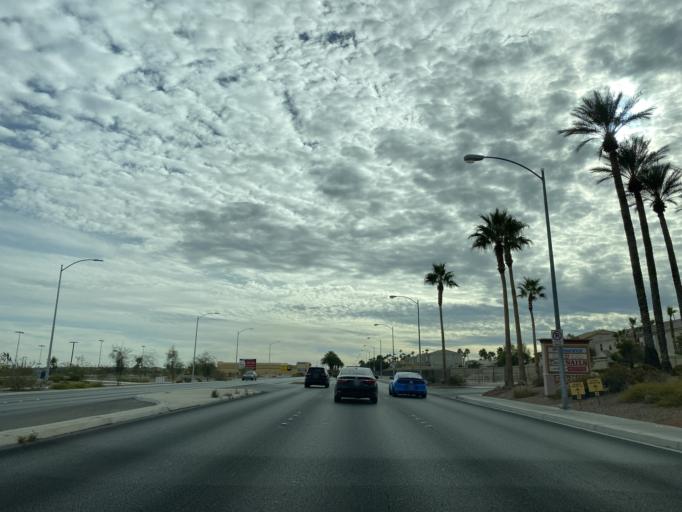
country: US
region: Nevada
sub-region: Clark County
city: Enterprise
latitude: 36.0534
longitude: -115.2792
